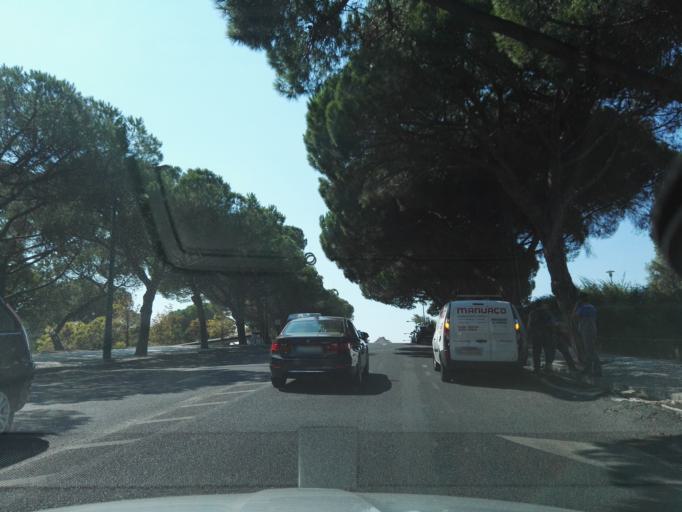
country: PT
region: Lisbon
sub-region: Lisbon
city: Lisbon
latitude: 38.7314
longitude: -9.1531
